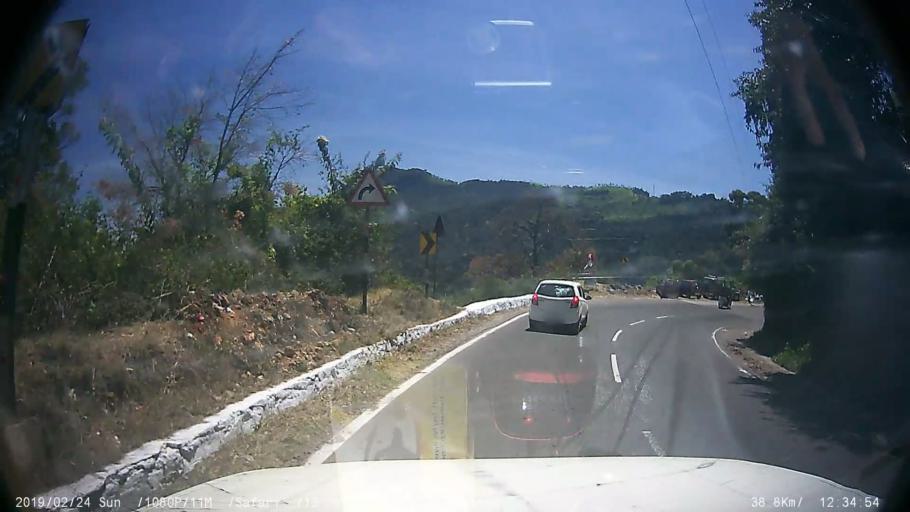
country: IN
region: Tamil Nadu
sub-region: Nilgiri
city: Wellington
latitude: 11.3361
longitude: 76.7988
